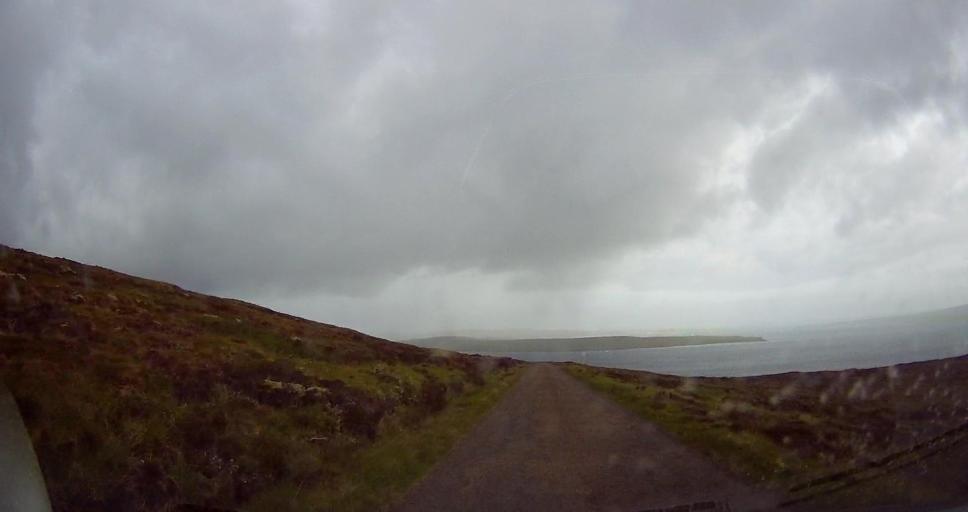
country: GB
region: Scotland
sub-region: Orkney Islands
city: Stromness
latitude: 58.8976
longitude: -3.2735
